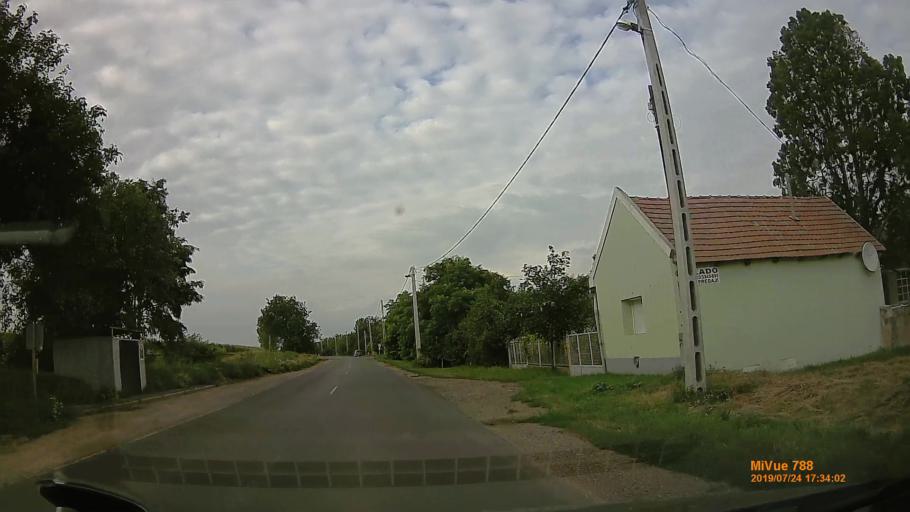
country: HU
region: Borsod-Abauj-Zemplen
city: Abaujszanto
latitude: 48.3002
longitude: 21.1956
